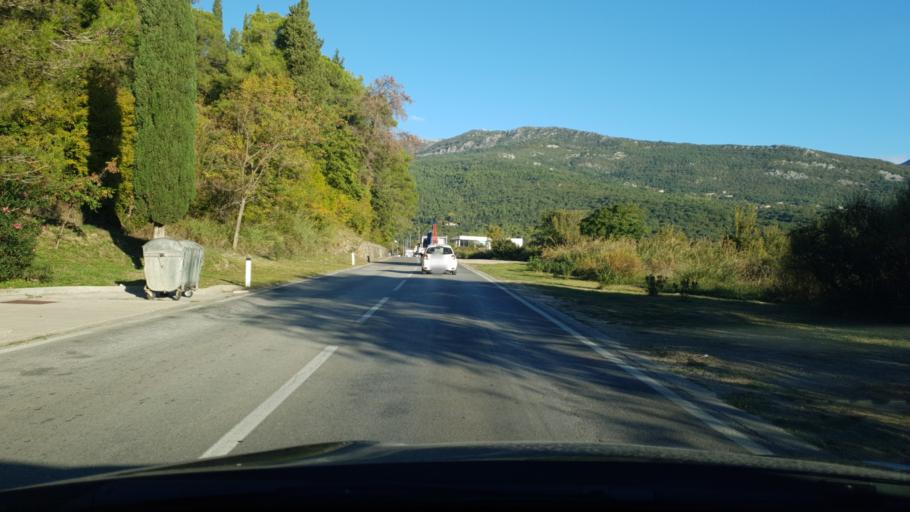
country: ME
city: Igalo
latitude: 42.4663
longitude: 18.4834
